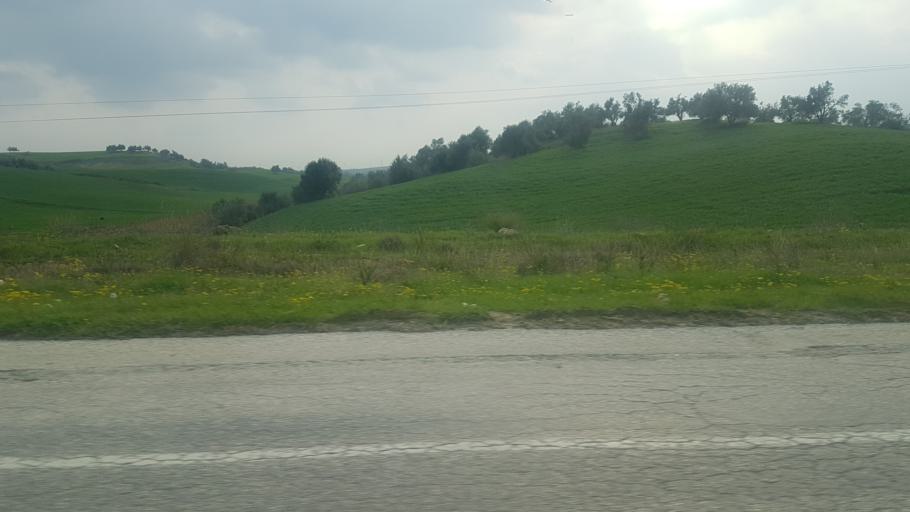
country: TR
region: Adana
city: Seyhan
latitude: 37.0457
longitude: 35.1808
